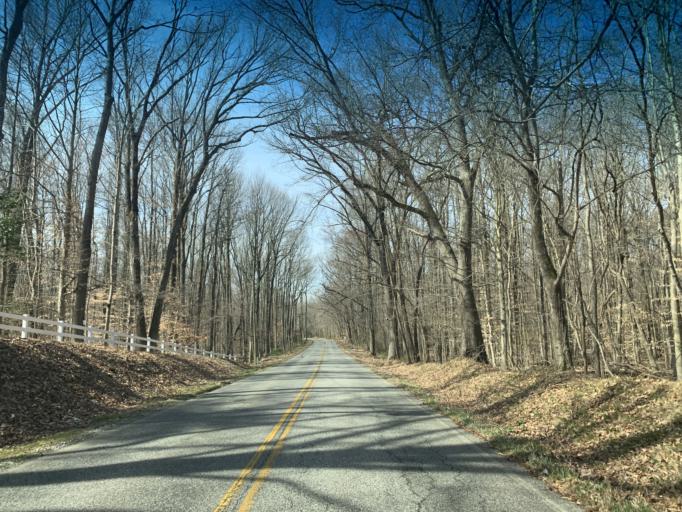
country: US
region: Maryland
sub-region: Cecil County
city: Charlestown
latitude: 39.5662
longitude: -76.0002
